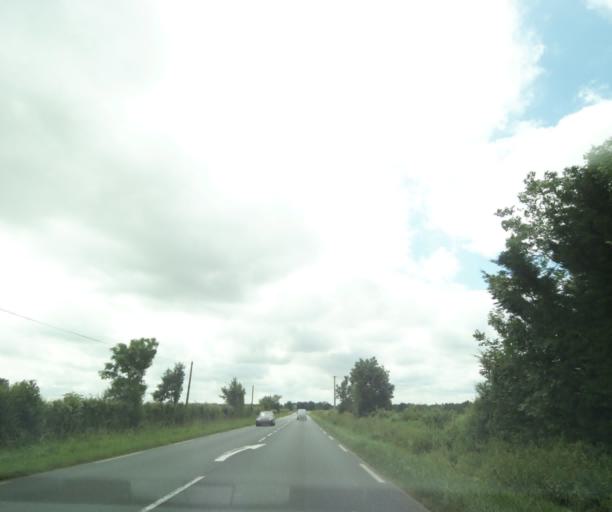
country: FR
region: Poitou-Charentes
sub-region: Departement des Deux-Sevres
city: Viennay
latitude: 46.7068
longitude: -0.2392
